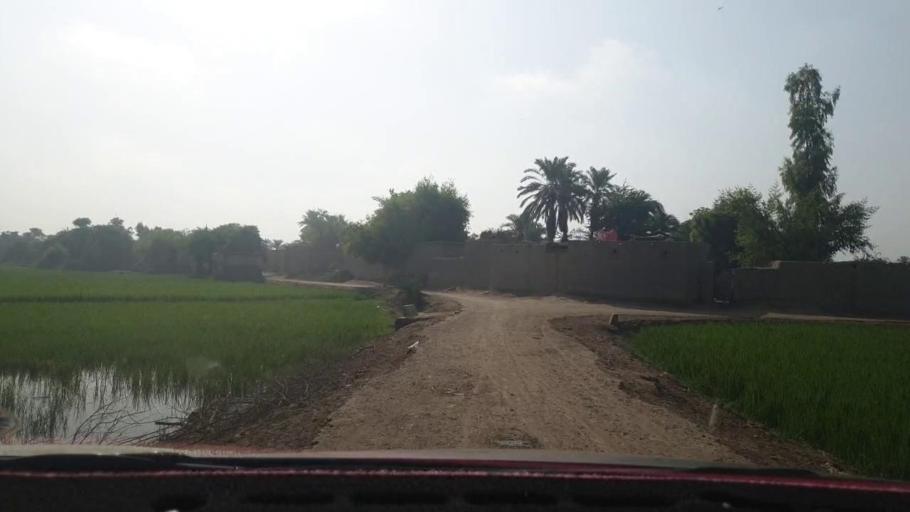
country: PK
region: Sindh
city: Nasirabad
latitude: 27.4545
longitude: 67.9614
